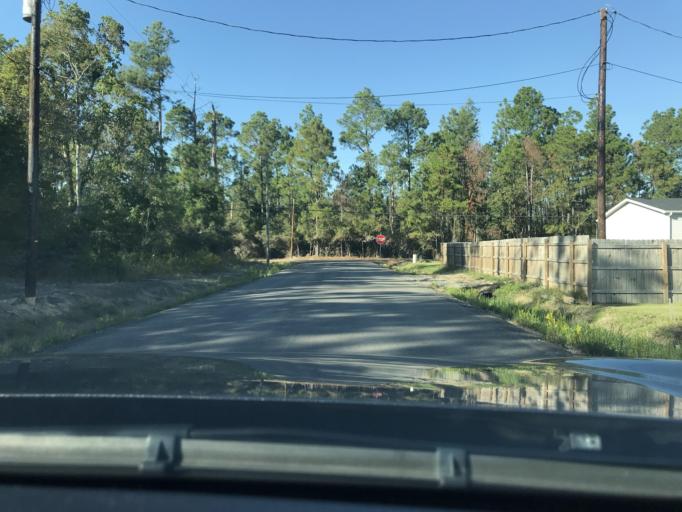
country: US
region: Louisiana
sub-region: Calcasieu Parish
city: Moss Bluff
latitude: 30.3220
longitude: -93.2688
